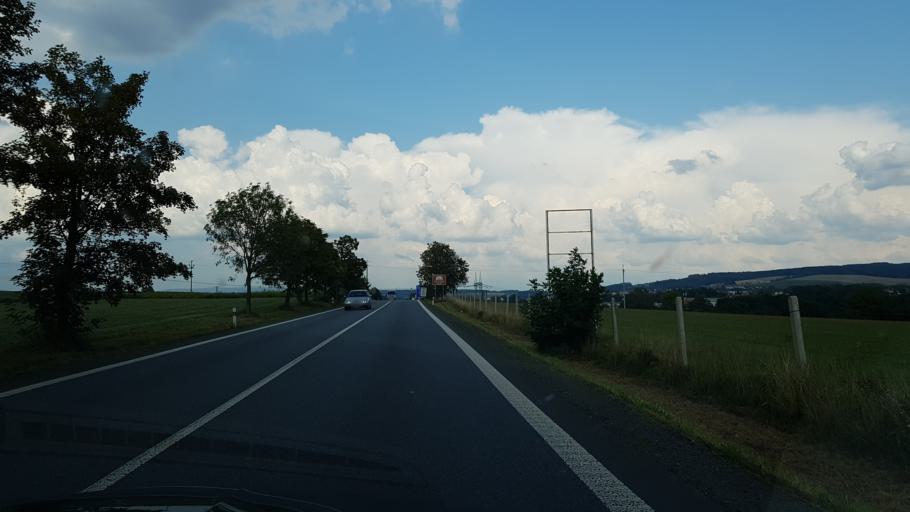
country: CZ
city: Doudleby nad Orlici
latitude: 50.1102
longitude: 16.2686
